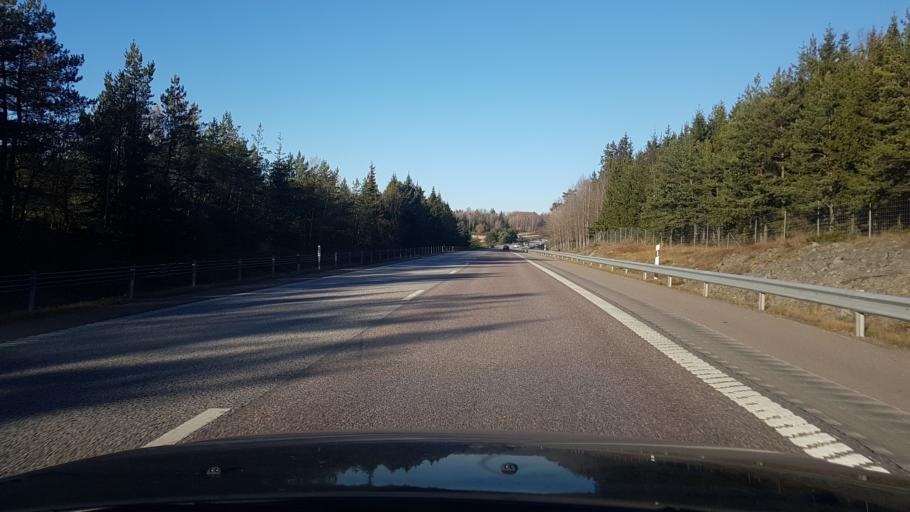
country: SE
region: Uppsala
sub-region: Uppsala Kommun
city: Alsike
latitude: 59.7745
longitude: 17.7848
